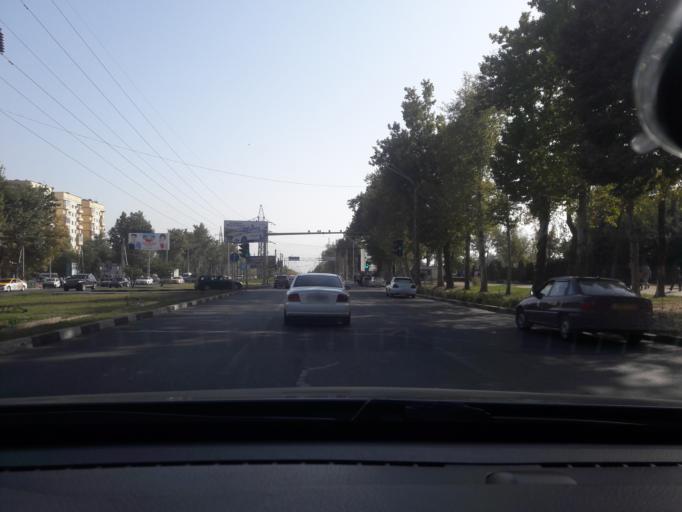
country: TJ
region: Dushanbe
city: Dushanbe
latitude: 38.5262
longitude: 68.7618
